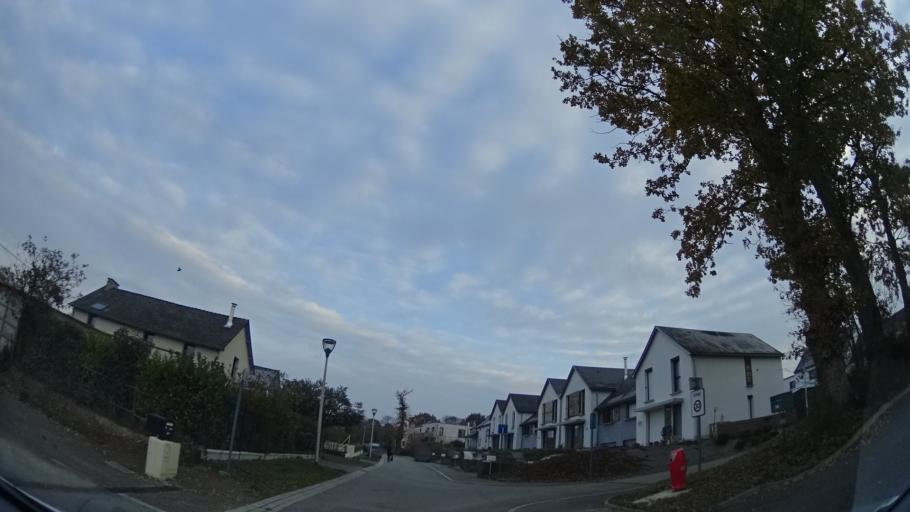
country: FR
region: Brittany
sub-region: Departement d'Ille-et-Vilaine
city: La Chapelle-des-Fougeretz
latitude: 48.1841
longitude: -1.7290
